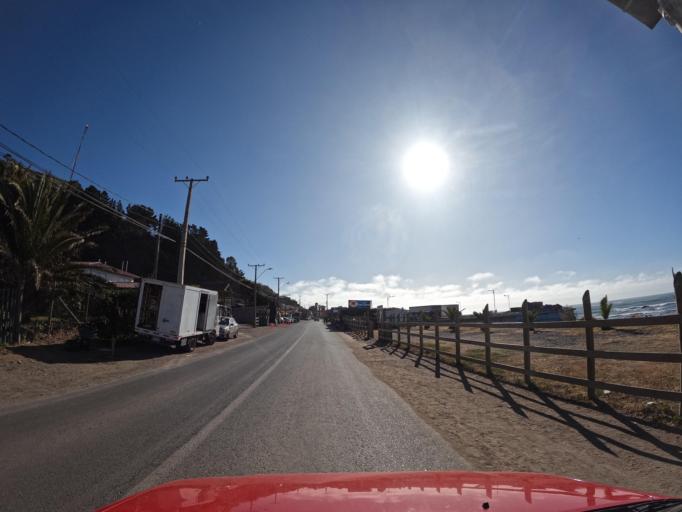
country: CL
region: Maule
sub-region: Provincia de Talca
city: Constitucion
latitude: -34.8853
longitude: -72.1639
